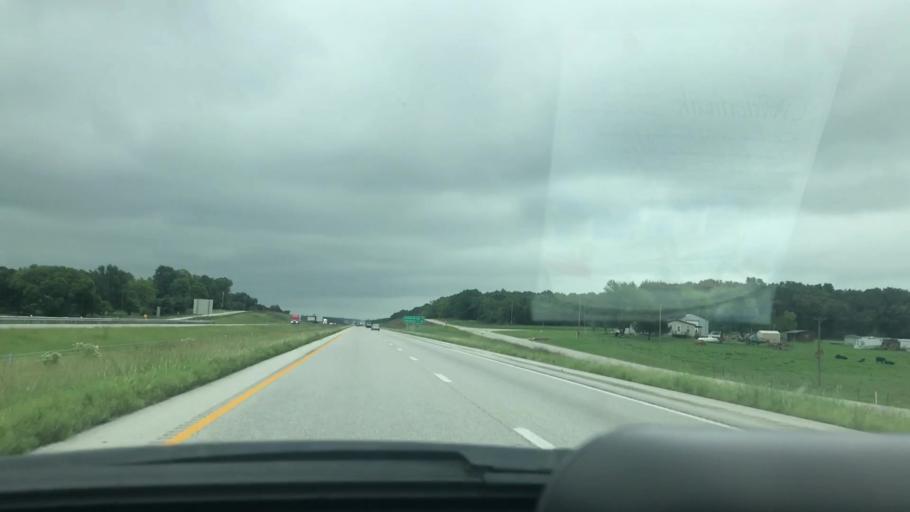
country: US
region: Missouri
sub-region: Jasper County
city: Carthage
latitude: 37.0818
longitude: -94.2976
